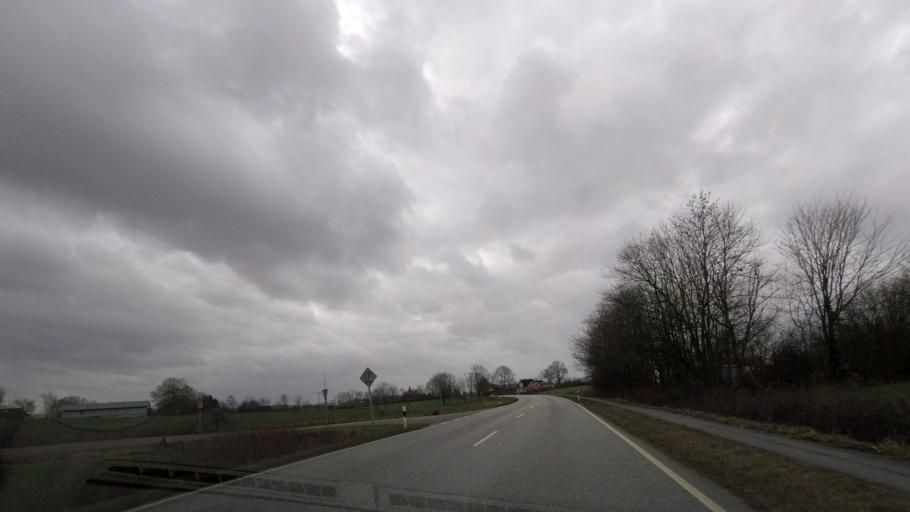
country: DE
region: Schleswig-Holstein
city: Twedt
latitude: 54.5960
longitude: 9.6740
